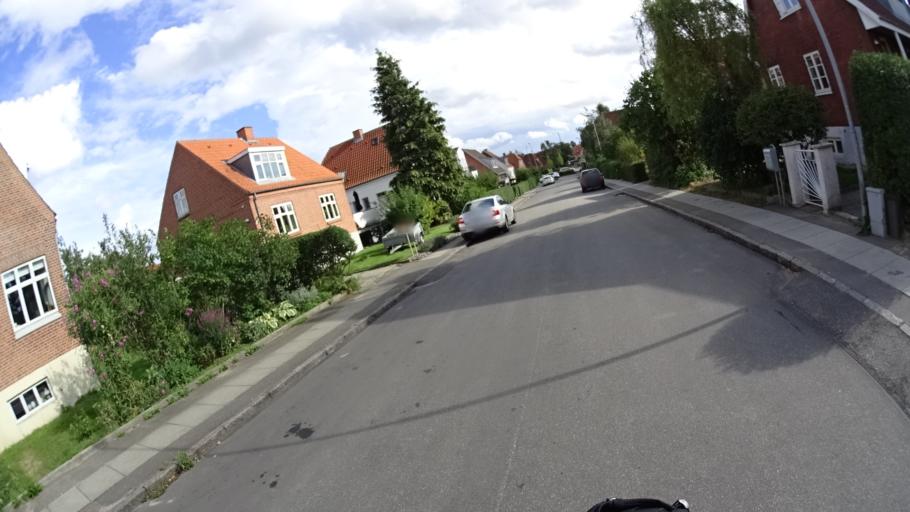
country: DK
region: Central Jutland
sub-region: Arhus Kommune
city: Stavtrup
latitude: 56.1498
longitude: 10.1604
